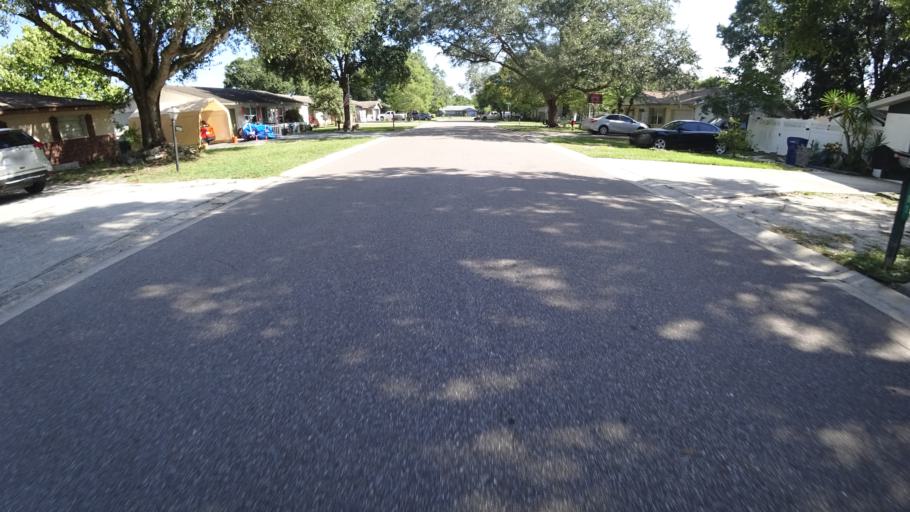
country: US
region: Florida
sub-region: Manatee County
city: Ellenton
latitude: 27.4982
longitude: -82.4809
